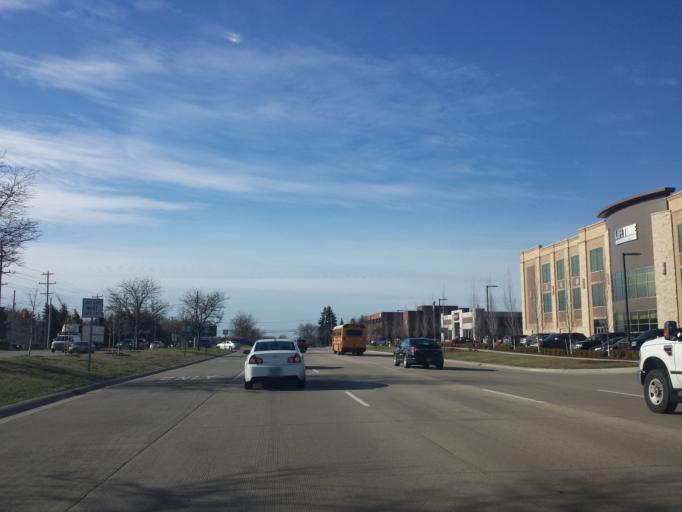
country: US
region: Michigan
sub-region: Oakland County
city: Bloomfield Hills
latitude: 42.5805
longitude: -83.2811
